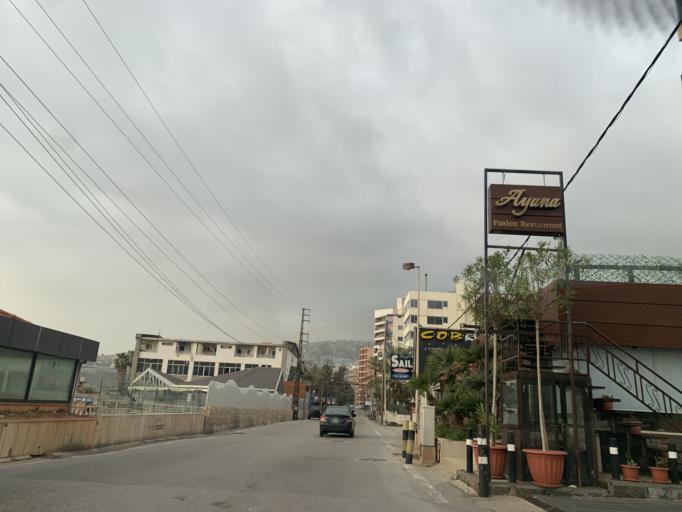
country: LB
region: Mont-Liban
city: Djounie
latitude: 34.0009
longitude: 35.6445
